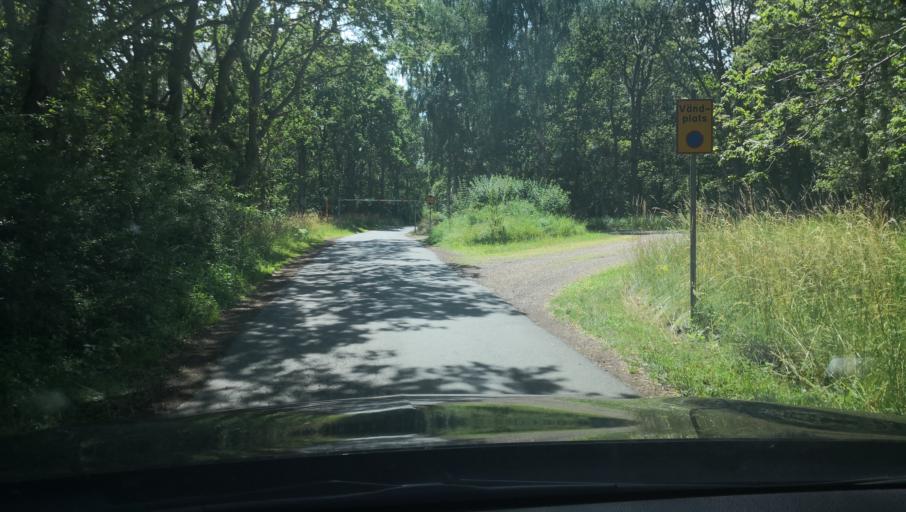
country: SE
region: Skane
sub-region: Ystads Kommun
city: Kopingebro
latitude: 55.3853
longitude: 14.1469
